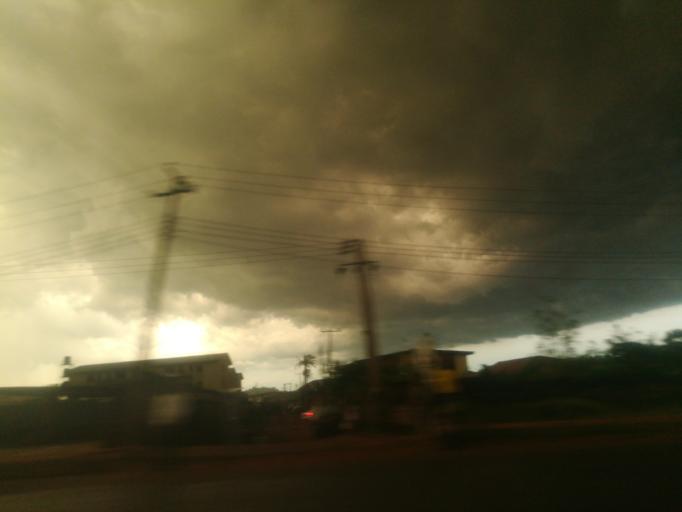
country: NG
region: Oyo
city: Ibadan
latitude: 7.4196
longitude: 3.9686
